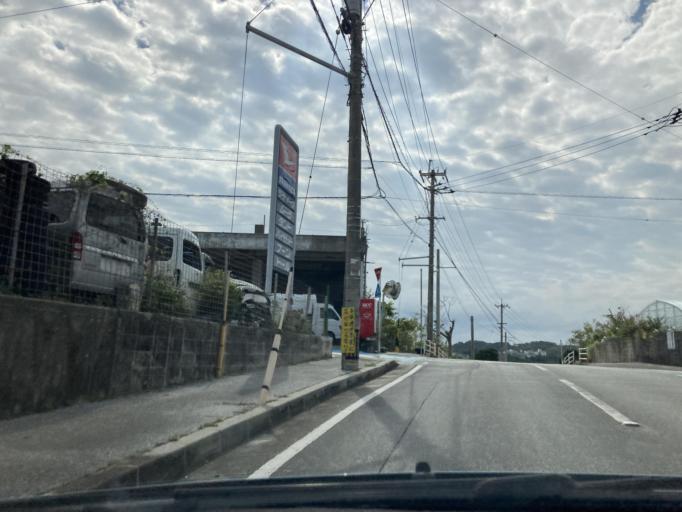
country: JP
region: Okinawa
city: Tomigusuku
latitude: 26.1866
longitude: 127.6962
